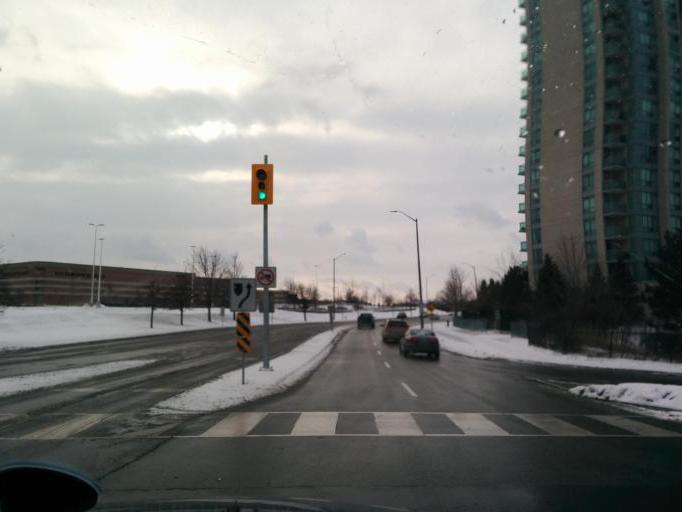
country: CA
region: Ontario
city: Mississauga
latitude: 43.5618
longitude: -79.7109
